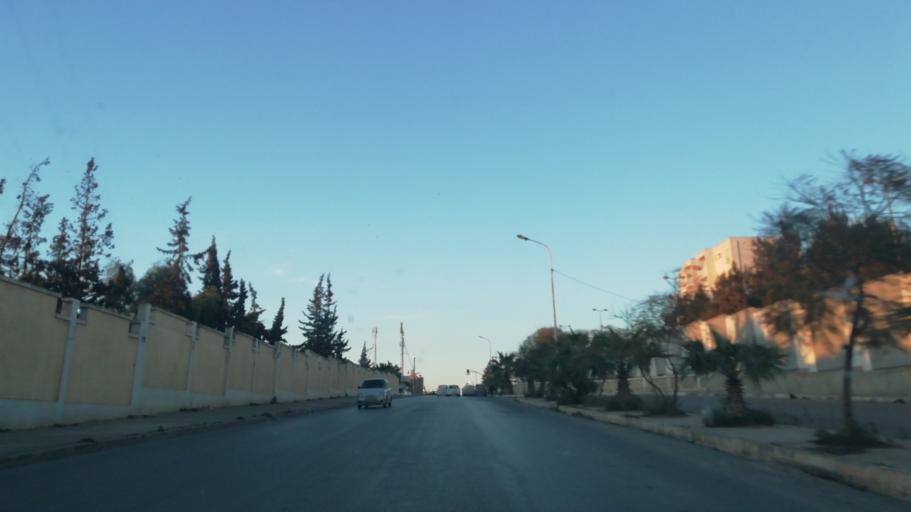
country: DZ
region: Oran
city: Bir el Djir
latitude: 35.7007
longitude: -0.5853
